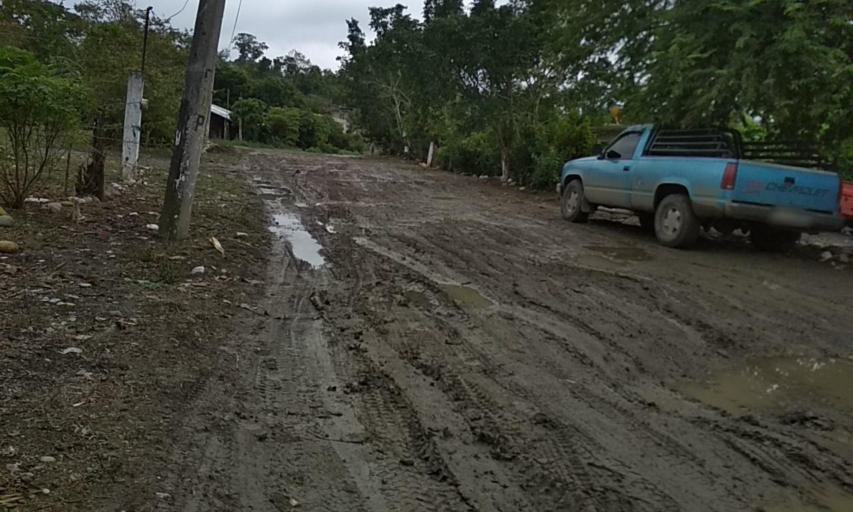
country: MX
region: Puebla
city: Espinal
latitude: 20.3201
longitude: -97.4175
